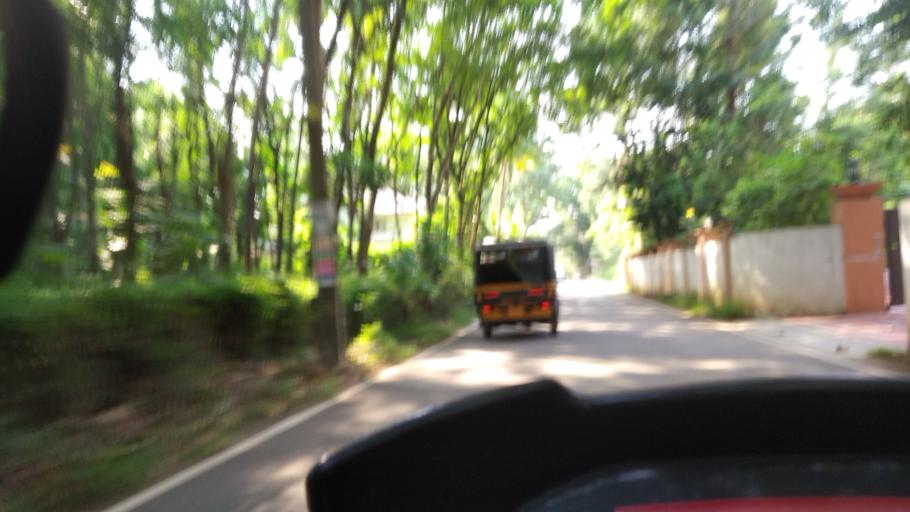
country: IN
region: Kerala
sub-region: Ernakulam
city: Piravam
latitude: 9.8678
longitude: 76.5046
